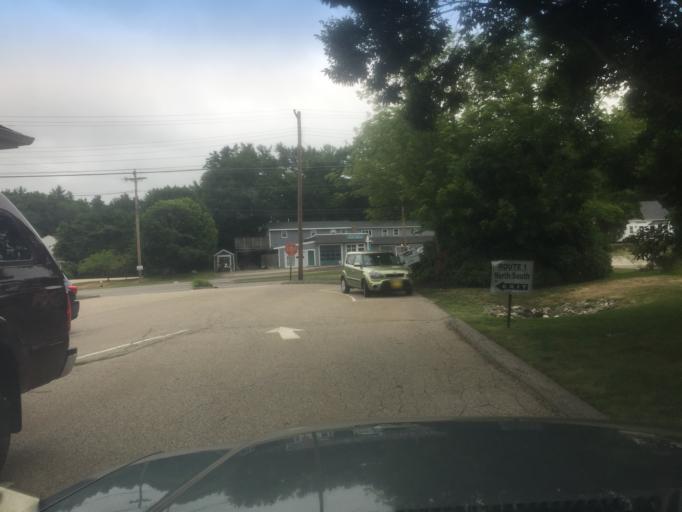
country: US
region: Maine
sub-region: York County
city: York Harbor
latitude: 43.1503
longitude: -70.6654
